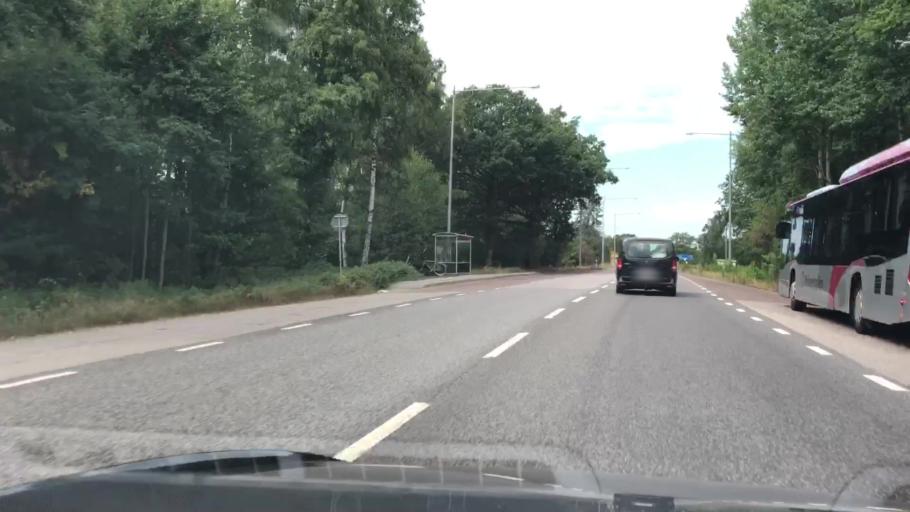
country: SE
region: Blekinge
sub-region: Karlskrona Kommun
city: Jaemjoe
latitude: 56.1852
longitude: 15.7187
